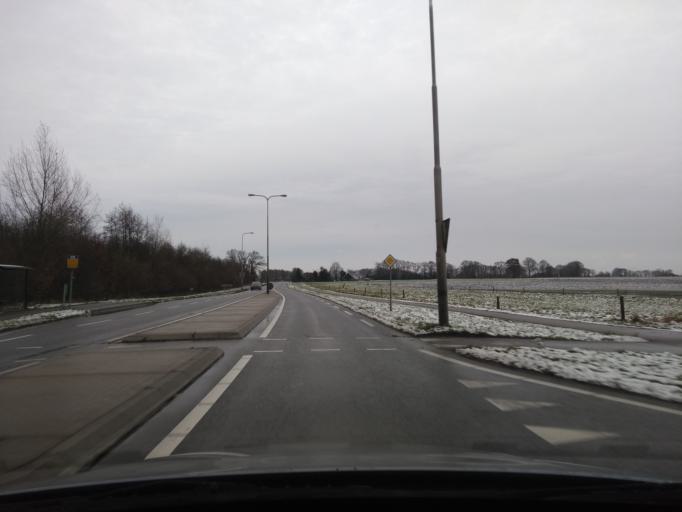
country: NL
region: Overijssel
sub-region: Gemeente Haaksbergen
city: Haaksbergen
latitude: 52.2008
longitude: 6.7306
